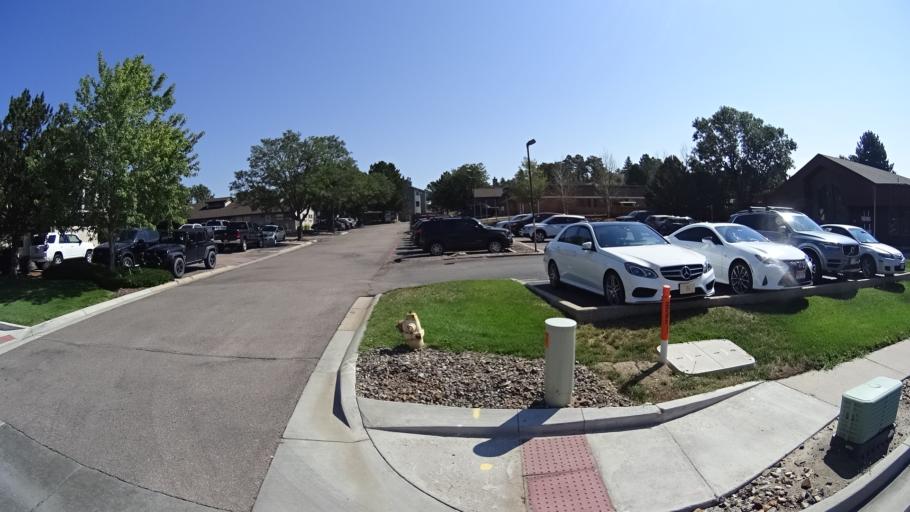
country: US
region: Colorado
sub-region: El Paso County
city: Air Force Academy
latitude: 38.9277
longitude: -104.8302
